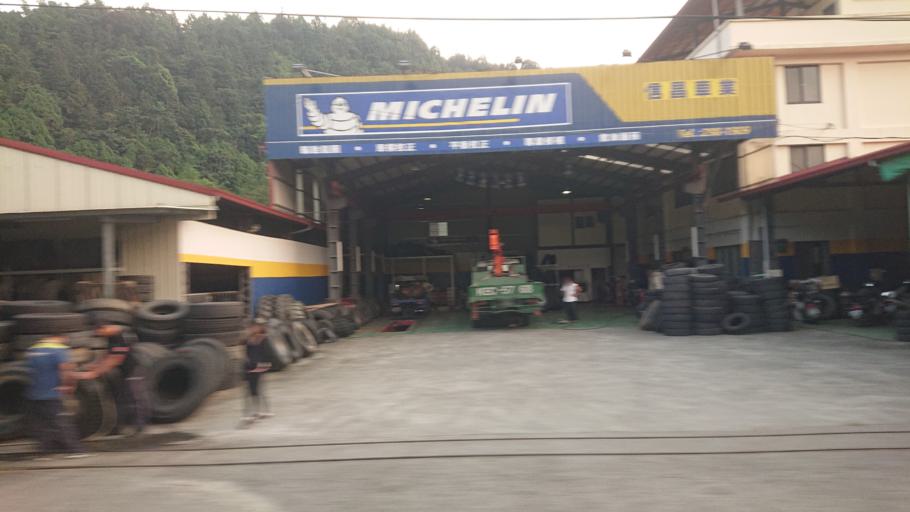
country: TW
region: Taiwan
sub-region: Nantou
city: Puli
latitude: 23.9725
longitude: 120.9950
